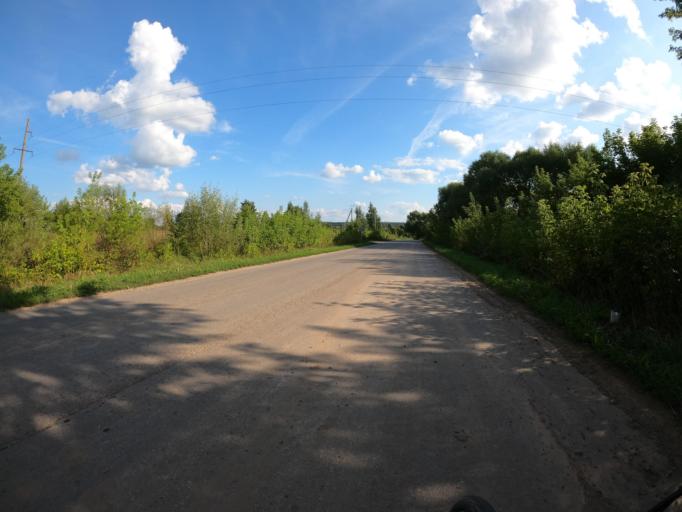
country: RU
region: Moskovskaya
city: Troitskoye
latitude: 55.1967
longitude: 38.4891
